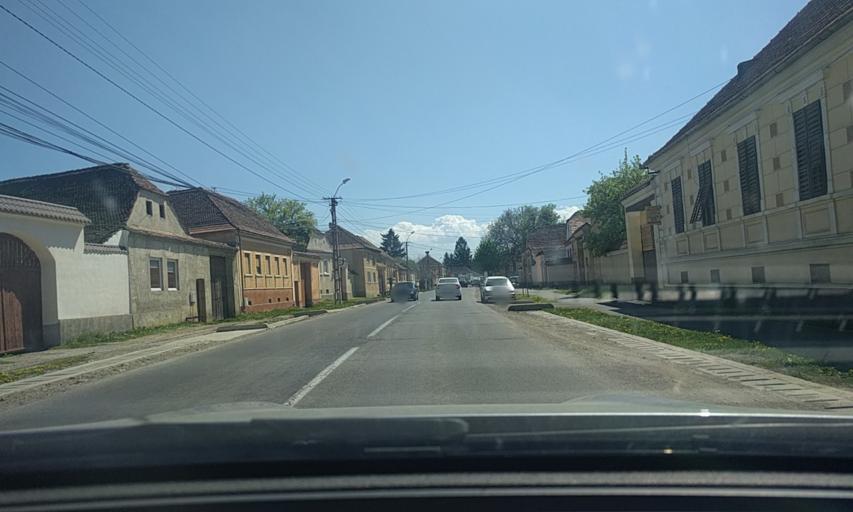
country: RO
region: Brasov
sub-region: Comuna Prejmer
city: Prejmer
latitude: 45.7172
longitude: 25.7779
